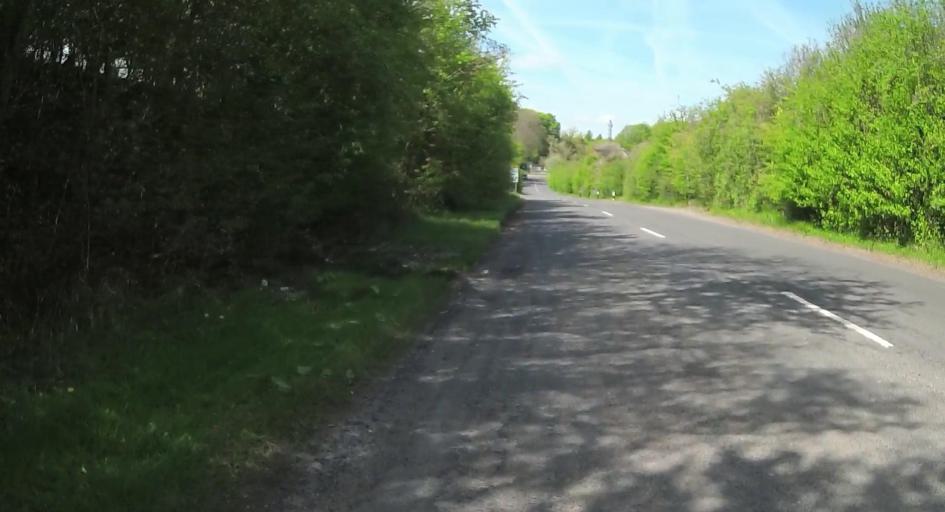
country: GB
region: England
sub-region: Hampshire
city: Winchester
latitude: 51.0871
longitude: -1.3288
